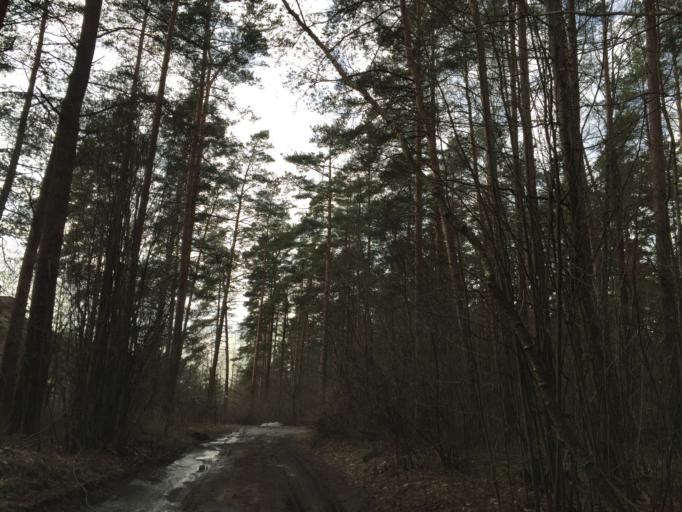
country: LV
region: Stopini
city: Ulbroka
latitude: 56.9216
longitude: 24.3001
